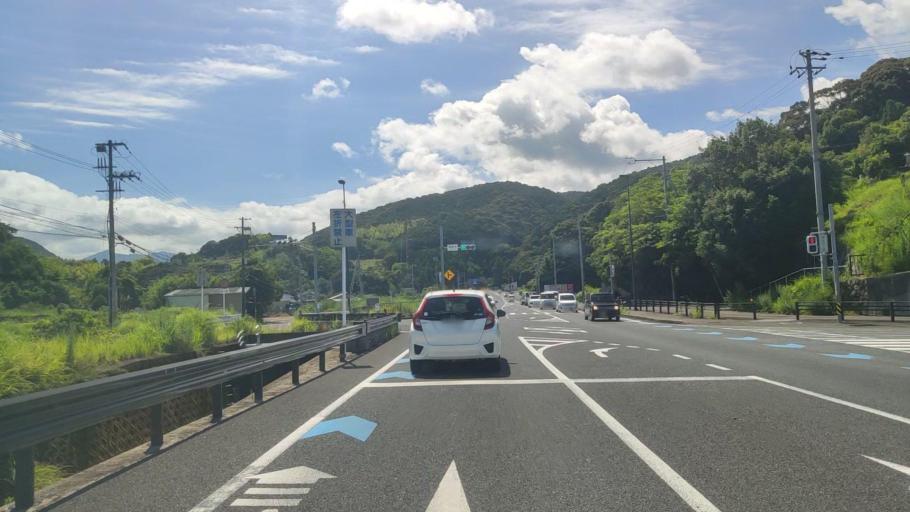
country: JP
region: Wakayama
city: Shingu
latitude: 33.7404
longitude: 135.9999
